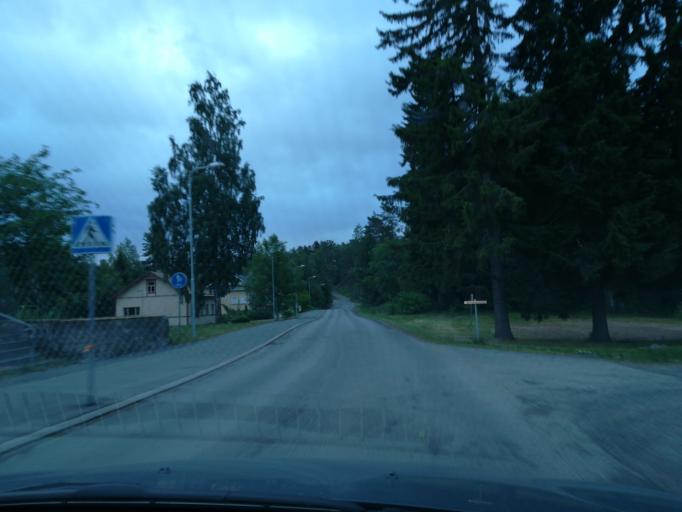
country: FI
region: Southern Savonia
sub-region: Mikkeli
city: Ristiina
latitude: 61.4996
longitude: 27.2682
